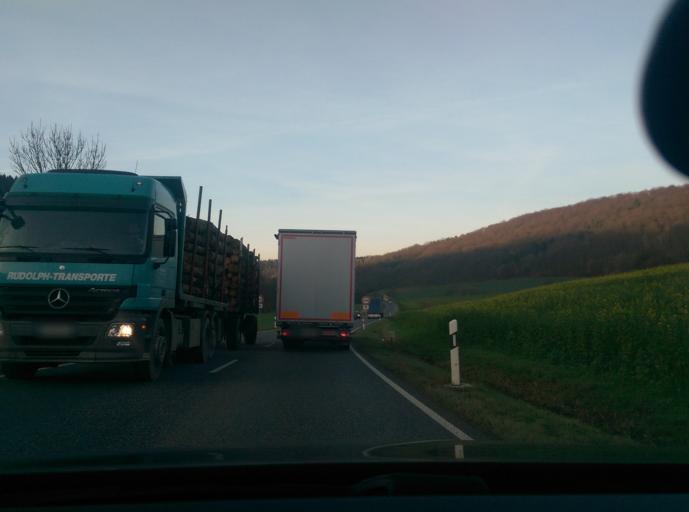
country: DE
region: Hesse
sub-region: Regierungsbezirk Kassel
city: Sontra
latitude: 51.0756
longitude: 9.9894
